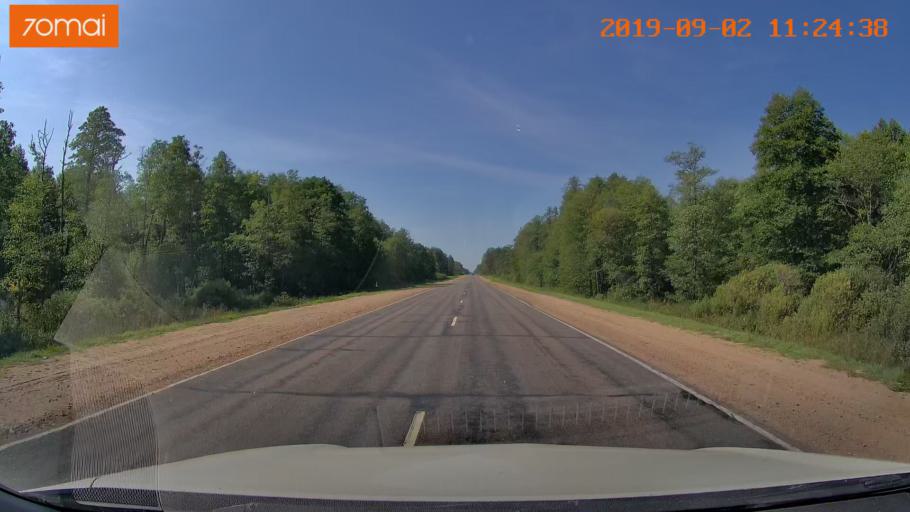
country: RU
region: Smolensk
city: Roslavl'
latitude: 54.0087
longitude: 32.9712
